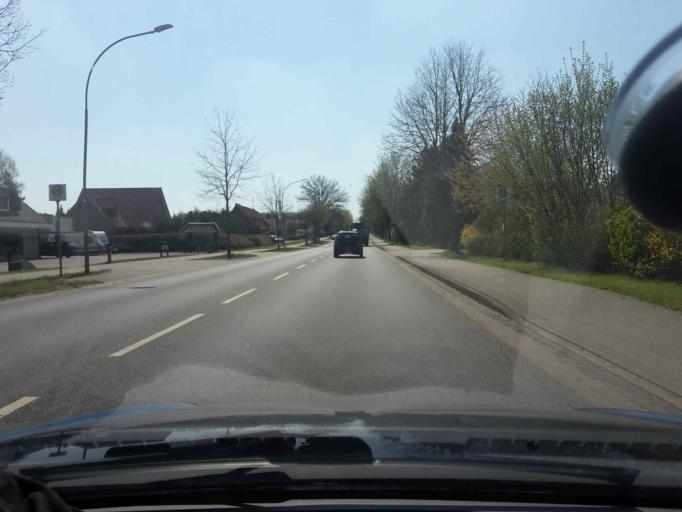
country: DE
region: Lower Saxony
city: Schneverdingen
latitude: 53.0795
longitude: 9.8632
